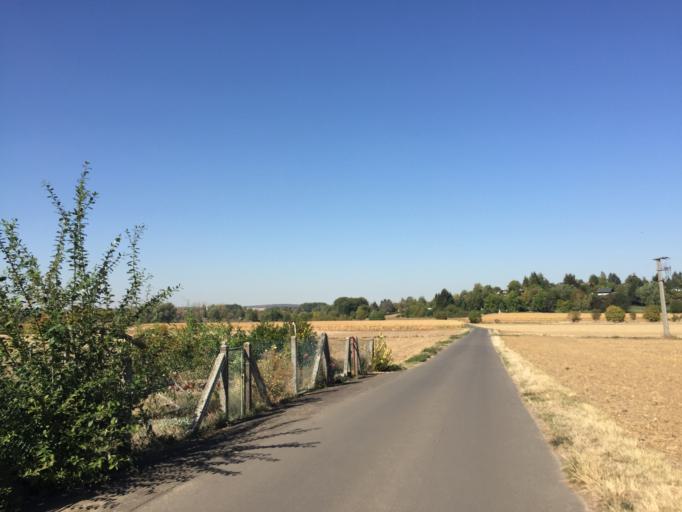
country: DE
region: Hesse
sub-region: Regierungsbezirk Giessen
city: Hungen
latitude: 50.4450
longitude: 8.9209
